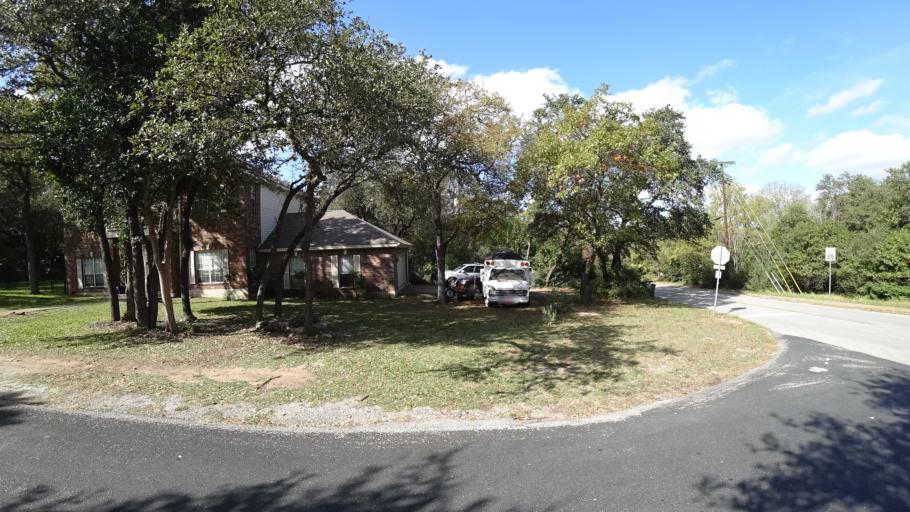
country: US
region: Texas
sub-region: Williamson County
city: Jollyville
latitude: 30.4261
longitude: -97.7794
